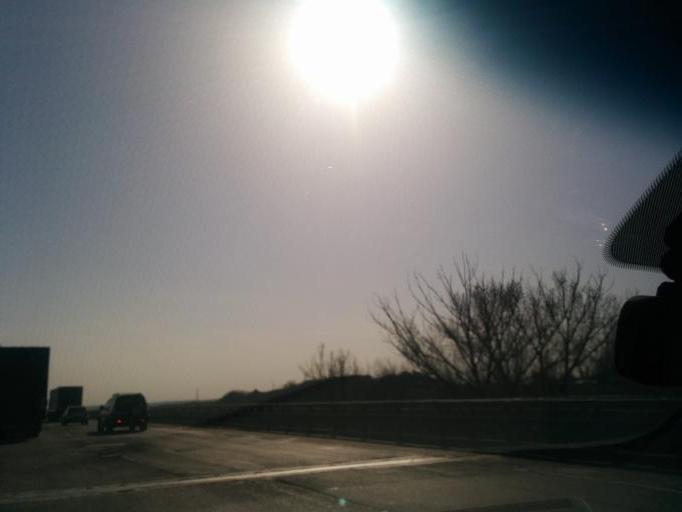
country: RU
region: Rostov
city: Mayskiy
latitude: 47.7005
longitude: 40.0906
